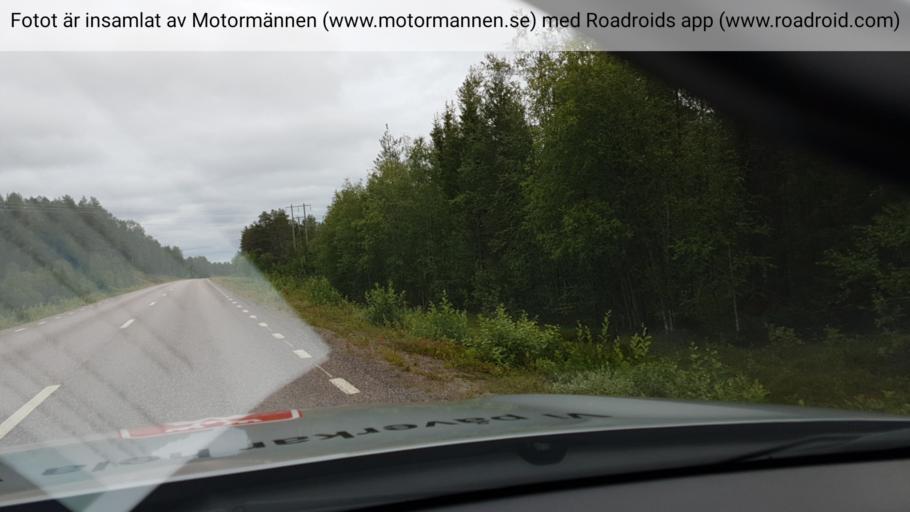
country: SE
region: Norrbotten
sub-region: Gallivare Kommun
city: Gaellivare
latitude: 67.0533
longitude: 21.2069
